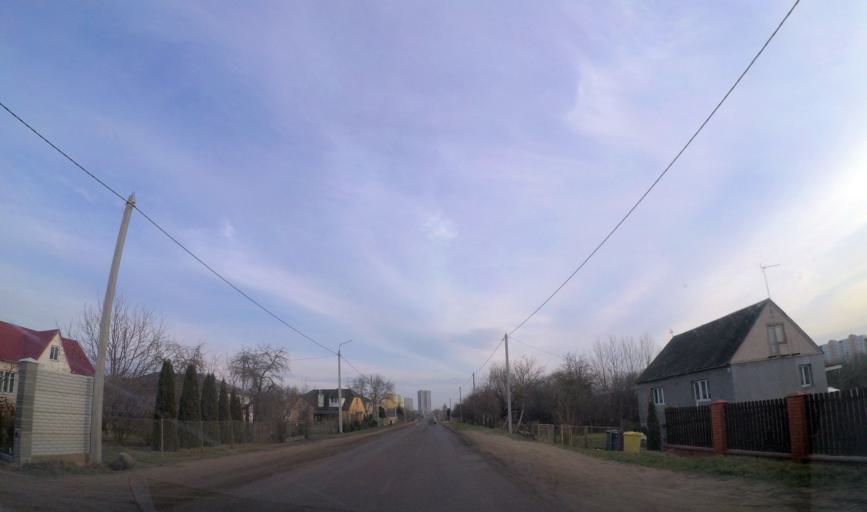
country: BY
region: Grodnenskaya
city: Hrodna
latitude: 53.7186
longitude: 23.8544
